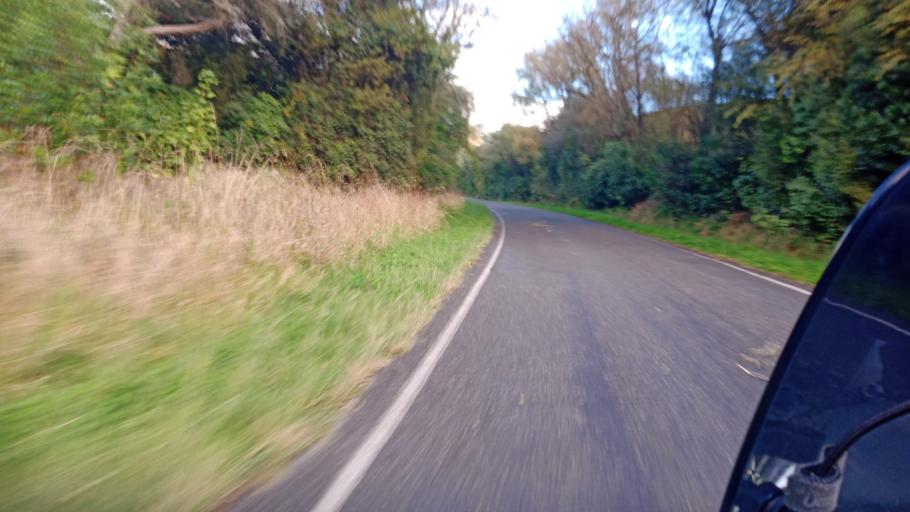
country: NZ
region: Gisborne
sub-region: Gisborne District
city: Gisborne
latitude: -38.5375
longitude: 177.5742
